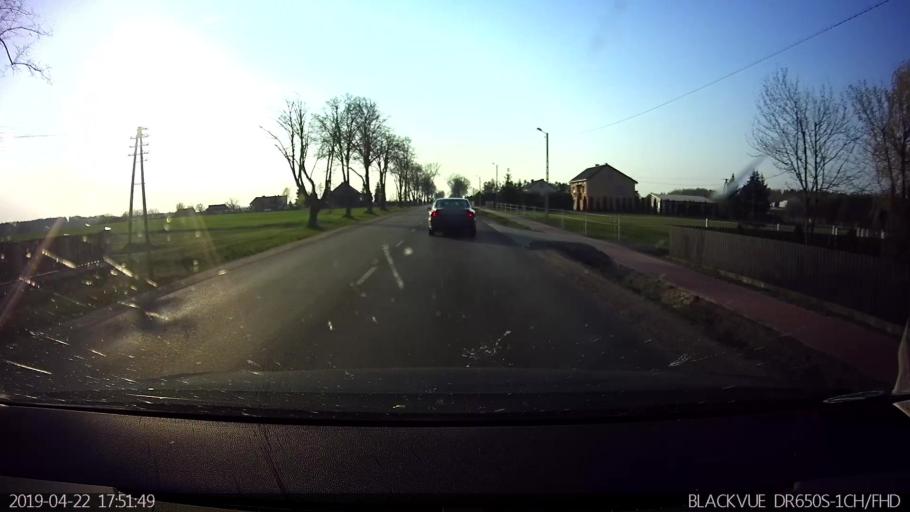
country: PL
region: Masovian Voivodeship
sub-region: Powiat wegrowski
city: Wegrow
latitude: 52.4371
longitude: 21.9892
